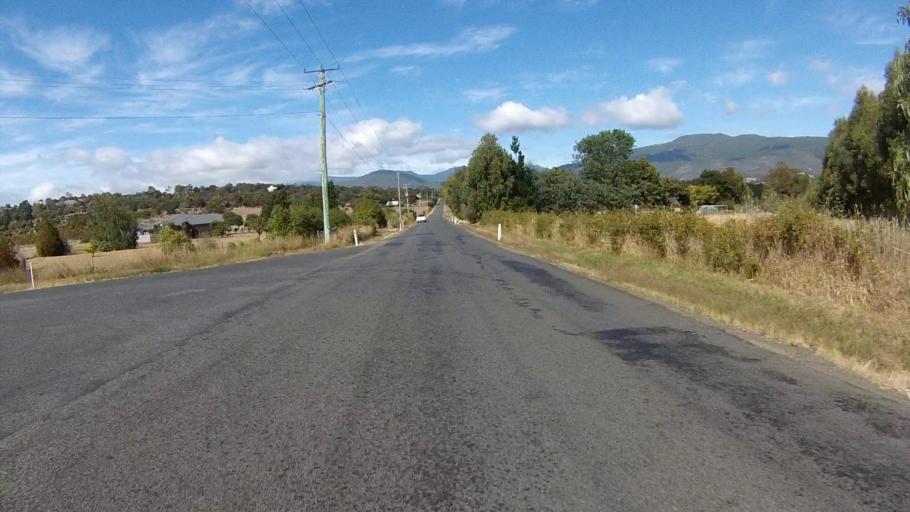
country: AU
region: Tasmania
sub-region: Brighton
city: Old Beach
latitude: -42.7635
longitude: 147.2778
